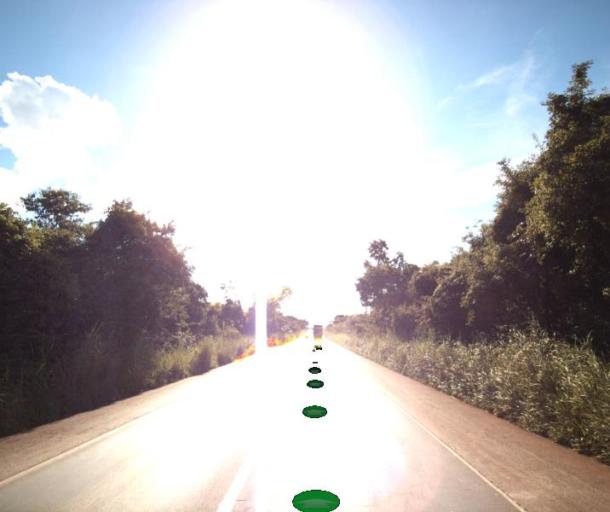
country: BR
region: Goias
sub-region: Rialma
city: Rialma
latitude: -15.3982
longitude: -49.5393
